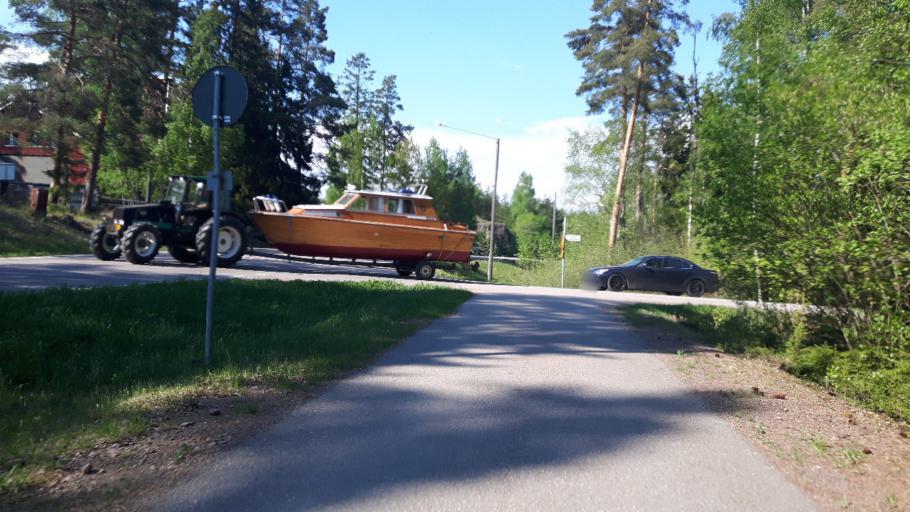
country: FI
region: Kymenlaakso
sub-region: Kotka-Hamina
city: Broby
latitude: 60.4953
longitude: 26.7714
